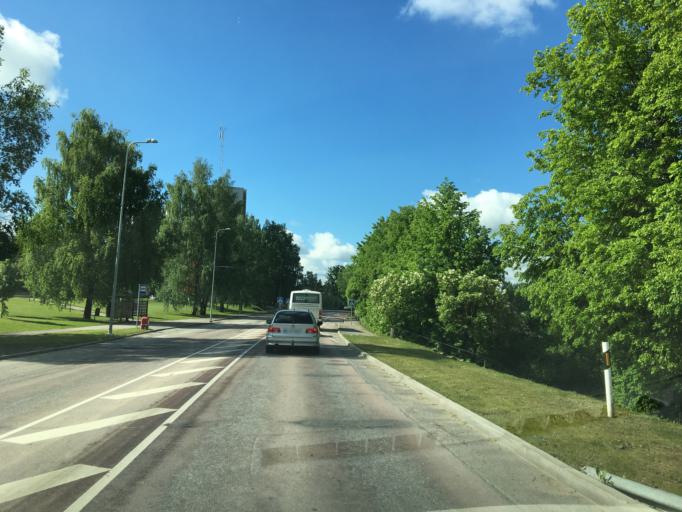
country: EE
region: Tartu
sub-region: Elva linn
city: Elva
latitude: 58.2353
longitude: 26.4109
